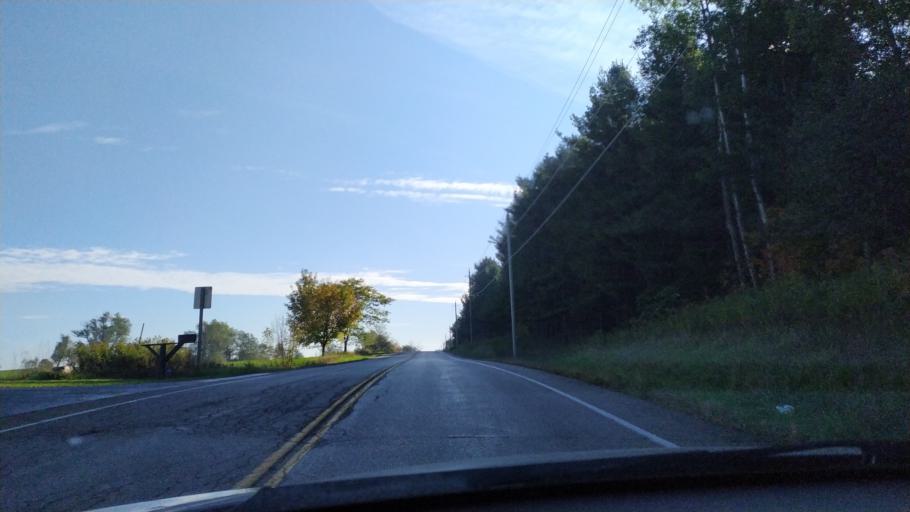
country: CA
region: Ontario
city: Waterloo
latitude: 43.4872
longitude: -80.6667
